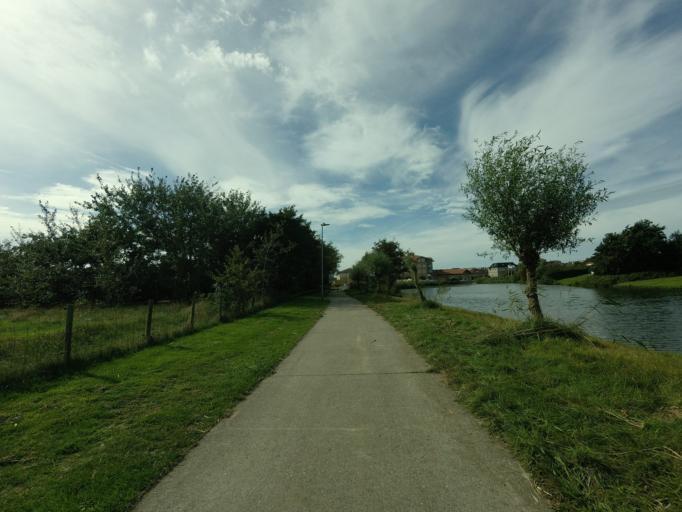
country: NL
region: North Holland
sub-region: Gemeente Texel
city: Den Burg
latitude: 53.0991
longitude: 4.7702
